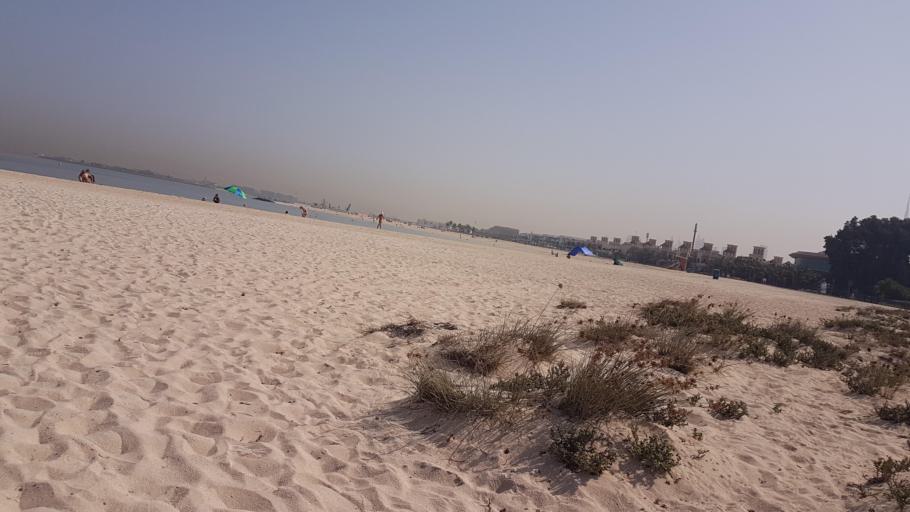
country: AE
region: Dubai
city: Dubai
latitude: 25.1801
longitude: 55.2197
